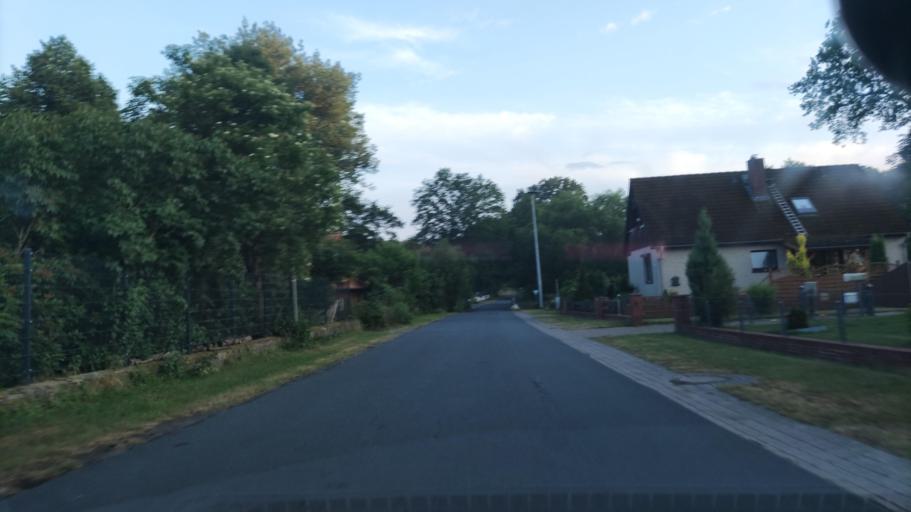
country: DE
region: Lower Saxony
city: Bispingen
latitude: 53.1046
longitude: 10.0573
